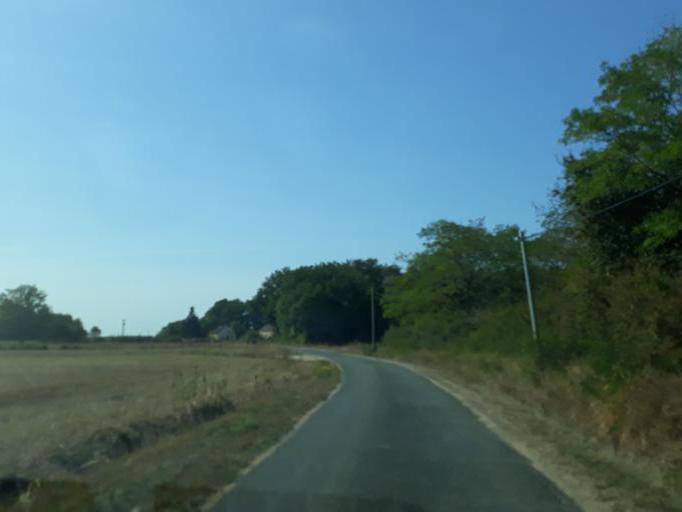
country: FR
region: Centre
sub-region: Departement de l'Indre
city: Chabris
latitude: 47.2634
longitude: 1.6297
